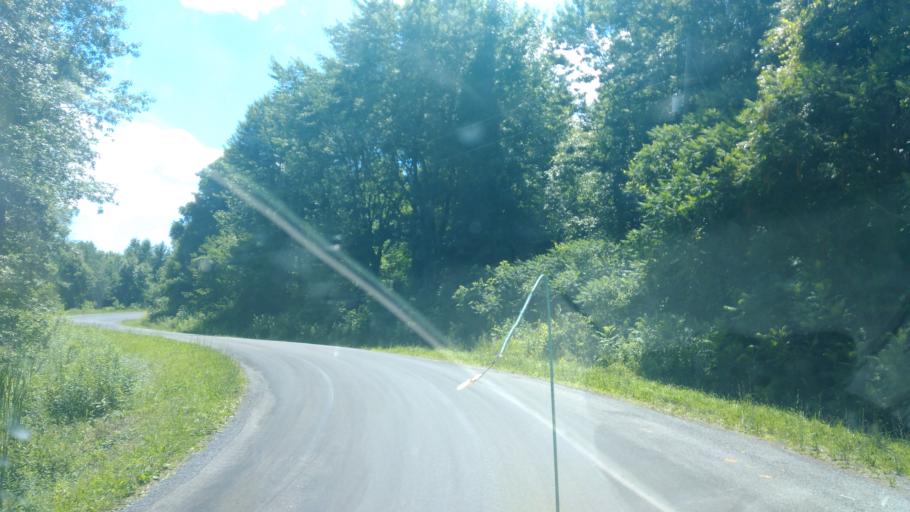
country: US
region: New York
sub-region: Wayne County
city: Lyons
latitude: 43.1504
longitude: -76.9644
